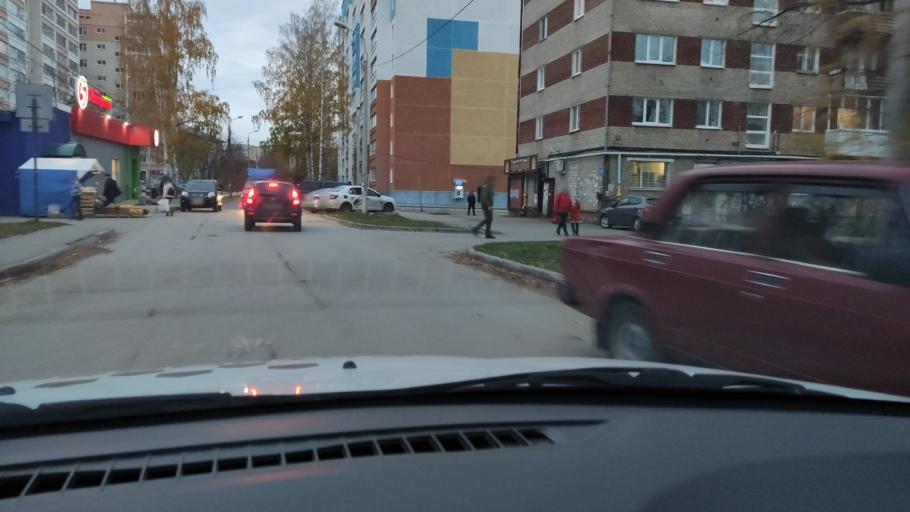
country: RU
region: Perm
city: Kondratovo
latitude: 58.0382
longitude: 56.1280
